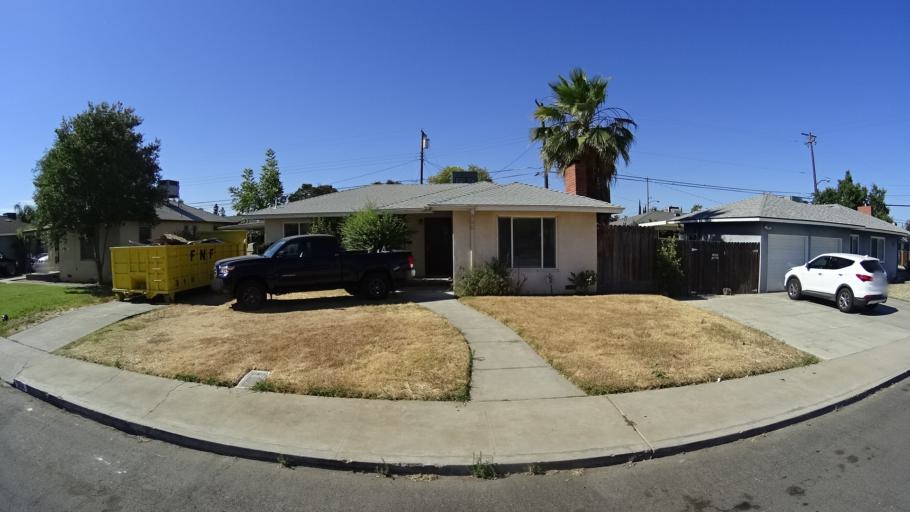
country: US
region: California
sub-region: Fresno County
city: Fresno
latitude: 36.7754
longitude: -119.7675
